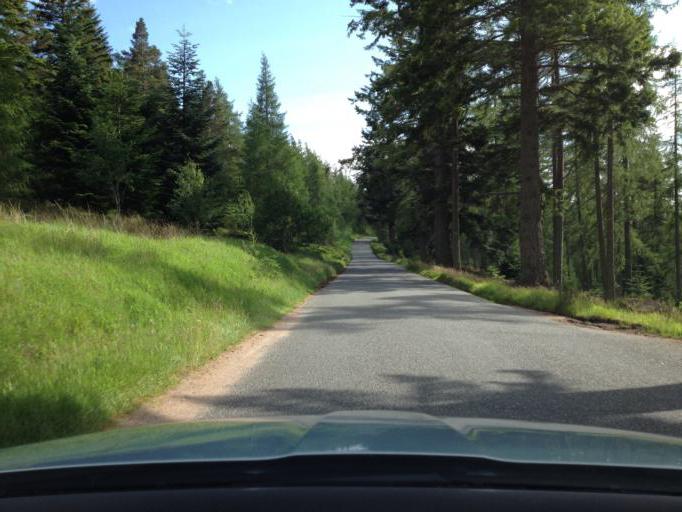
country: GB
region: Scotland
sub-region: Aberdeenshire
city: Banchory
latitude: 56.9574
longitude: -2.5812
